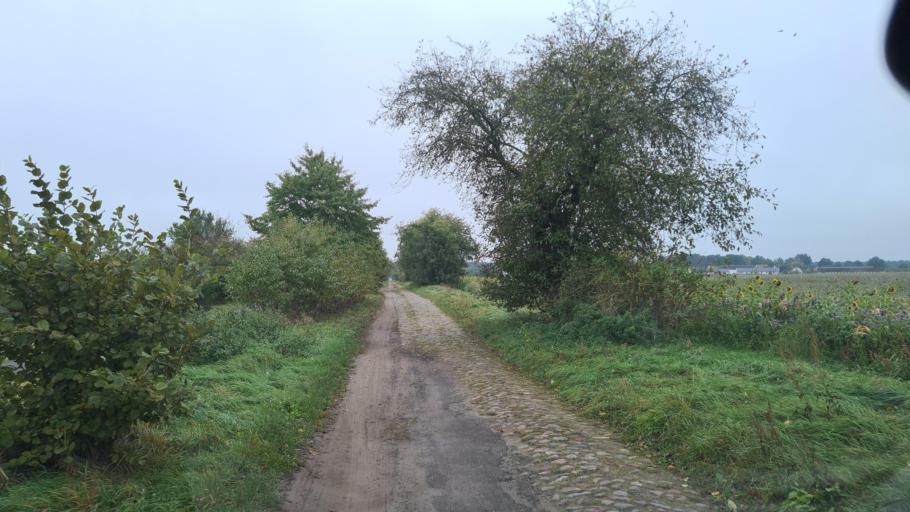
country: DE
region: Brandenburg
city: Furstenwalde
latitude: 52.4110
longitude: 14.0345
